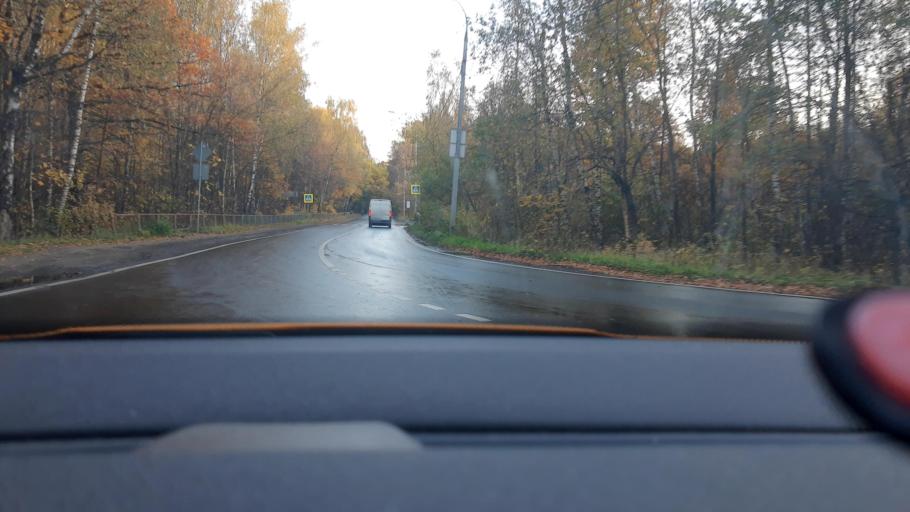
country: RU
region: Moskovskaya
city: Bogorodskoye
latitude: 55.8281
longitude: 37.7468
